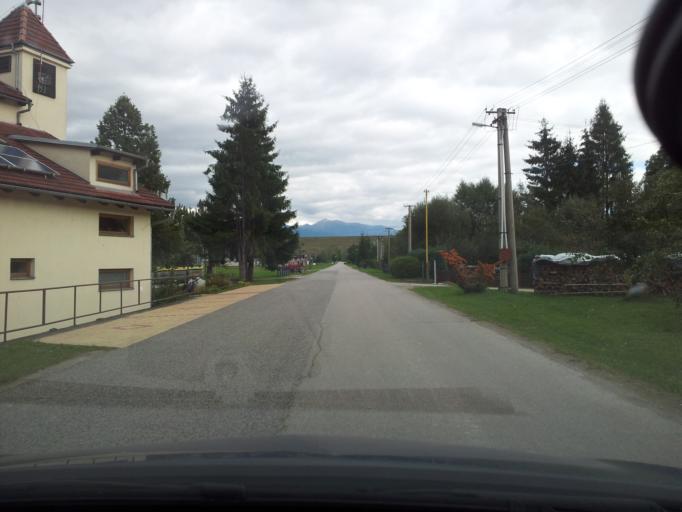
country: SK
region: Zilinsky
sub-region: Okres Liptovsky Mikulas
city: Liptovsky Mikulas
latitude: 49.0928
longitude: 19.4741
